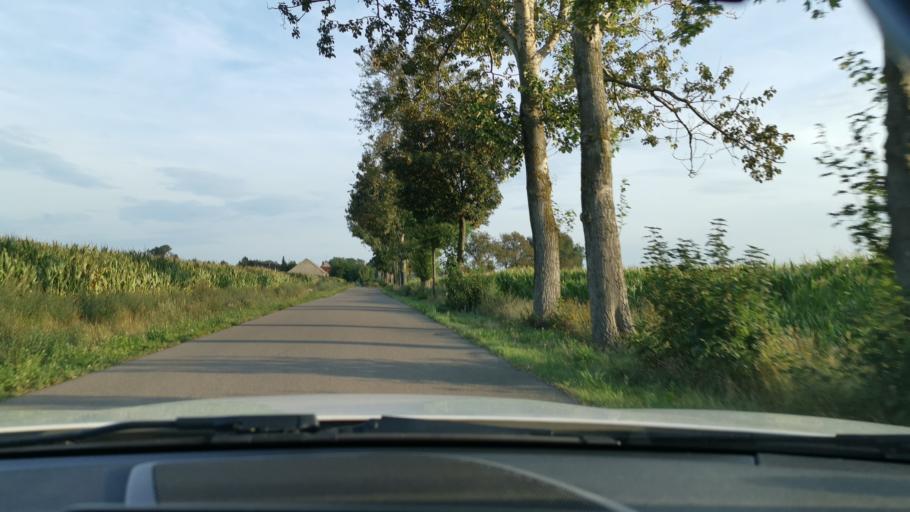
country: DE
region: Brandenburg
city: Juterbog
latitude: 51.9325
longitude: 13.1386
